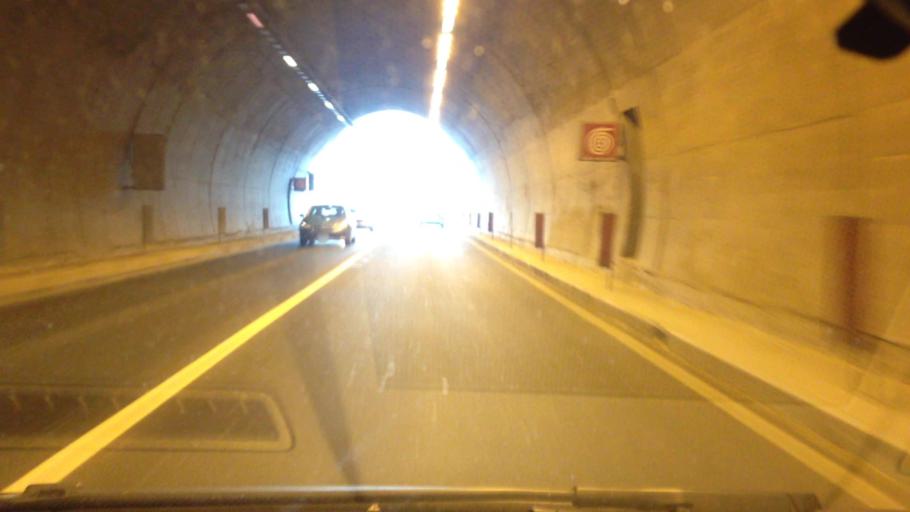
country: IT
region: Piedmont
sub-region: Provincia di Asti
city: Piano-Molini d'Isola
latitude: 44.8388
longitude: 8.1966
